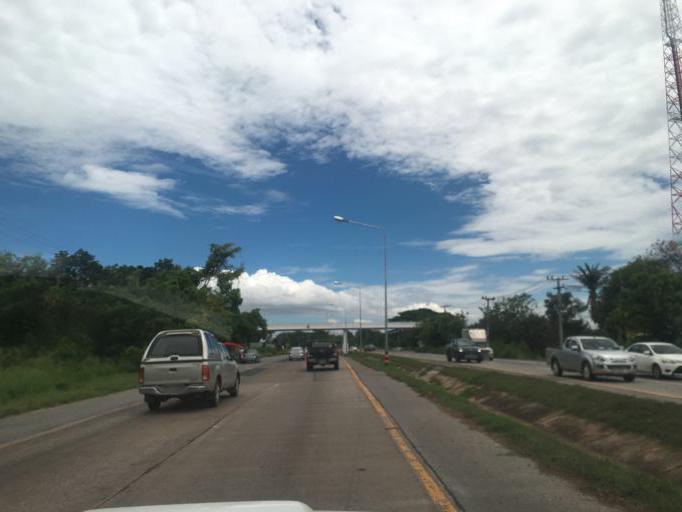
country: TH
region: Khon Kaen
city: Nam Phong
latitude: 16.6605
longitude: 102.8011
